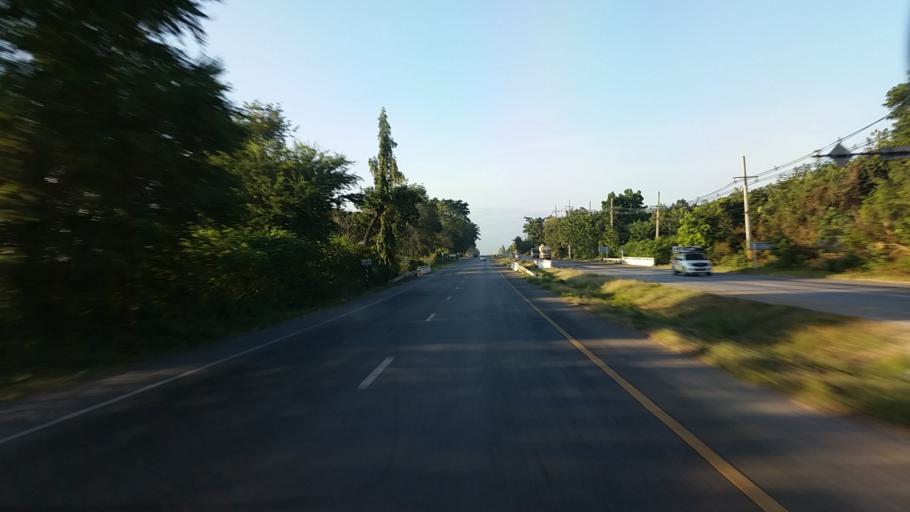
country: TH
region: Lop Buri
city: Chai Badan
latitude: 15.1992
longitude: 101.0849
